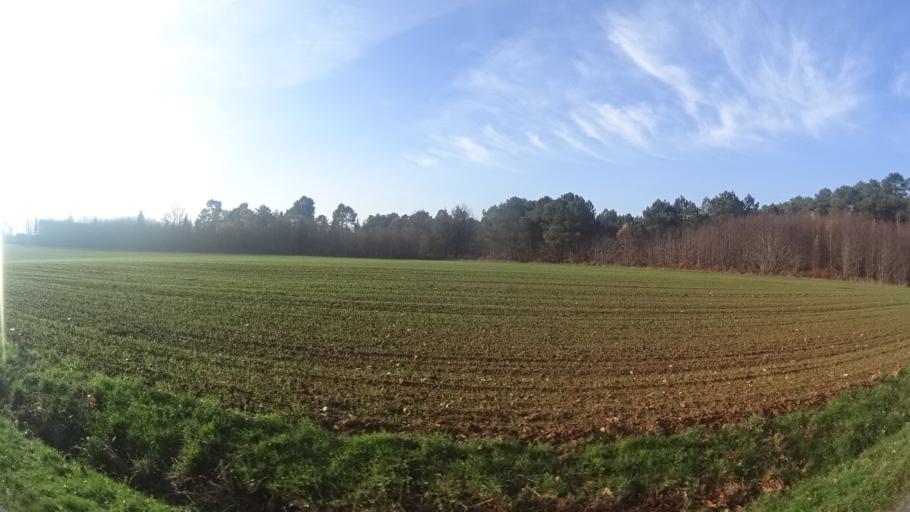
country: FR
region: Brittany
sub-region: Departement du Morbihan
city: Allaire
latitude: 47.6183
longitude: -2.1505
